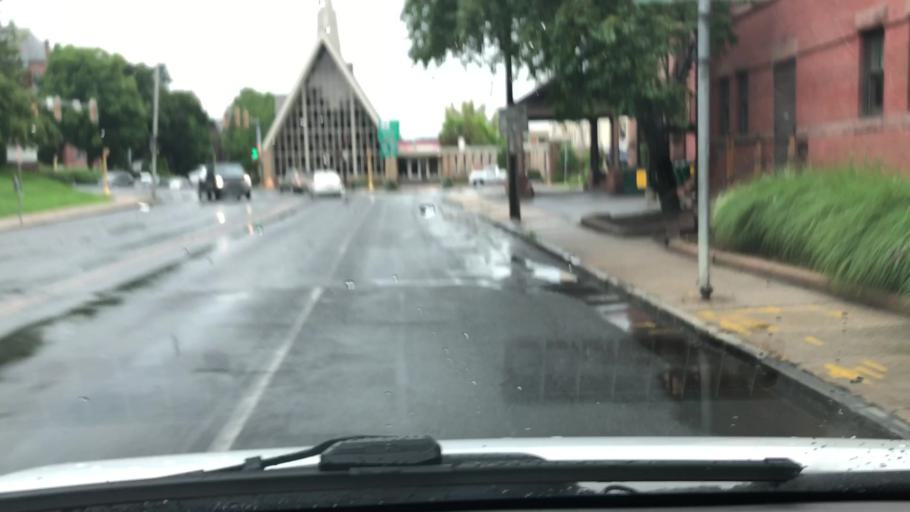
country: US
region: Massachusetts
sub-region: Hampshire County
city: Northampton
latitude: 42.3171
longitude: -72.6338
